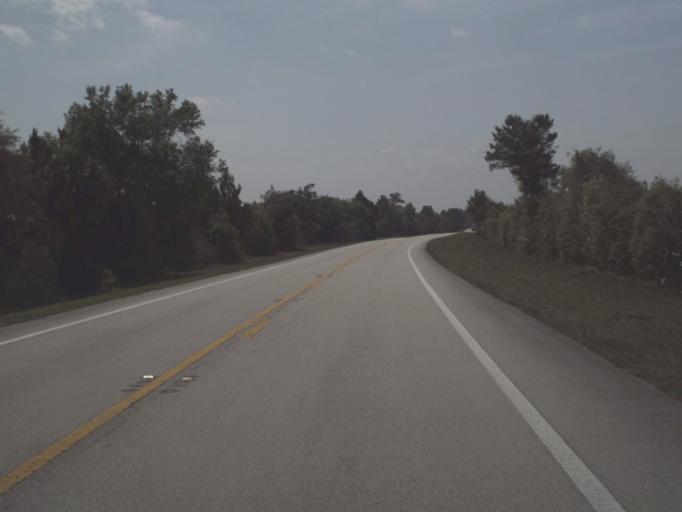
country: US
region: Florida
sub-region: Lake County
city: Astor
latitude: 29.2375
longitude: -81.6464
